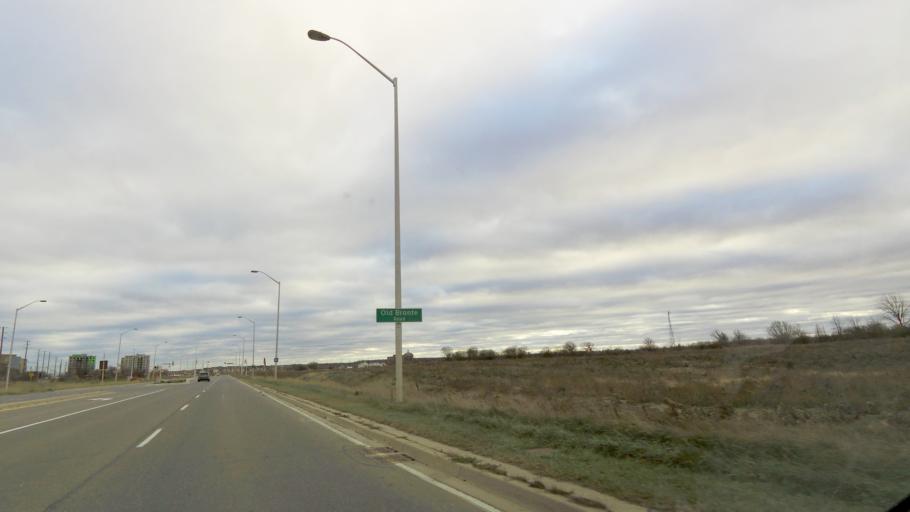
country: CA
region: Ontario
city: Burlington
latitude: 43.4394
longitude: -79.7823
